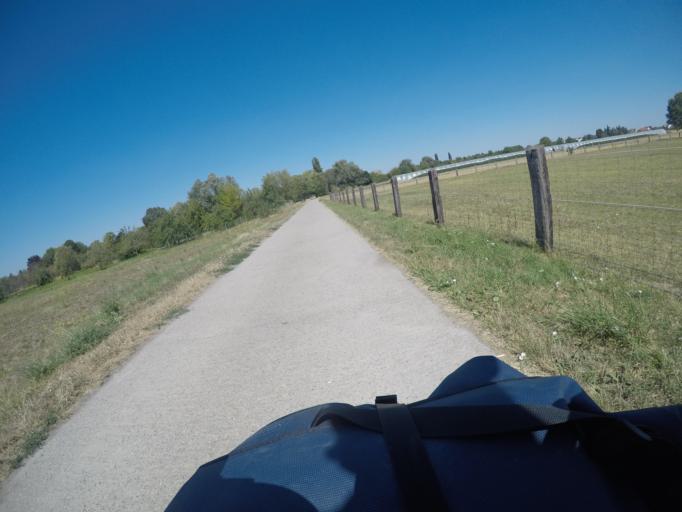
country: DE
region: Baden-Wuerttemberg
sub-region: Karlsruhe Region
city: Altlussheim
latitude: 49.3001
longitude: 8.4919
